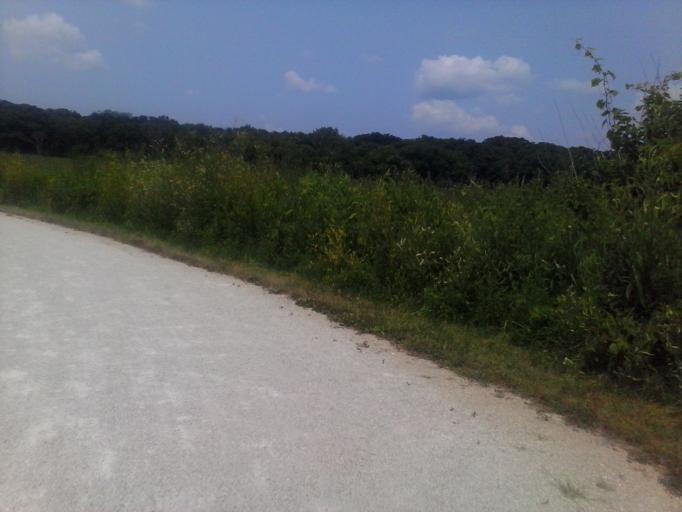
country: US
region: Illinois
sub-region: DuPage County
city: Naperville
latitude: 41.8131
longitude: -88.1349
